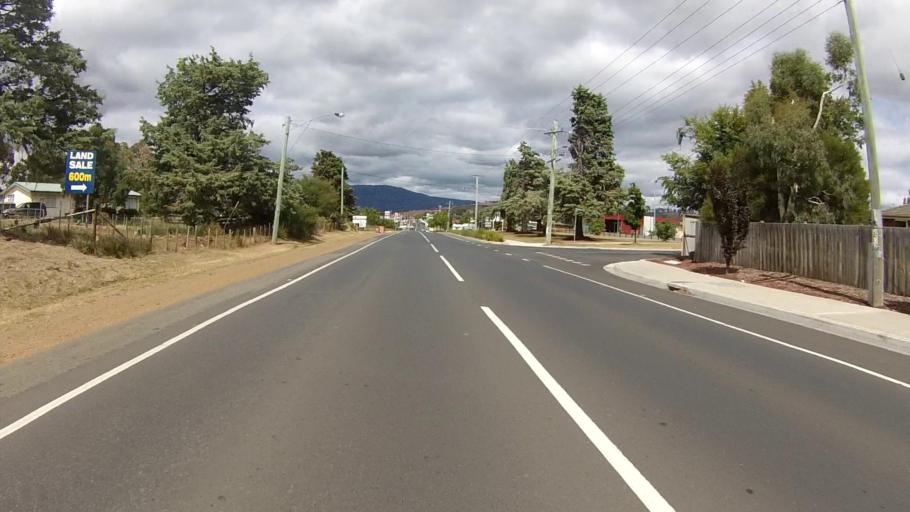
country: AU
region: Tasmania
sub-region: Brighton
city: Bridgewater
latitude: -42.6949
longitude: 147.2559
